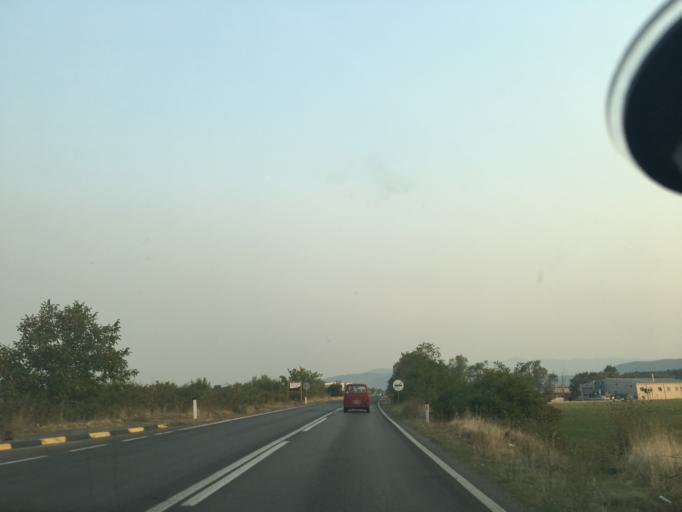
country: ME
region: Danilovgrad
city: Danilovgrad
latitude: 42.5371
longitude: 19.1128
